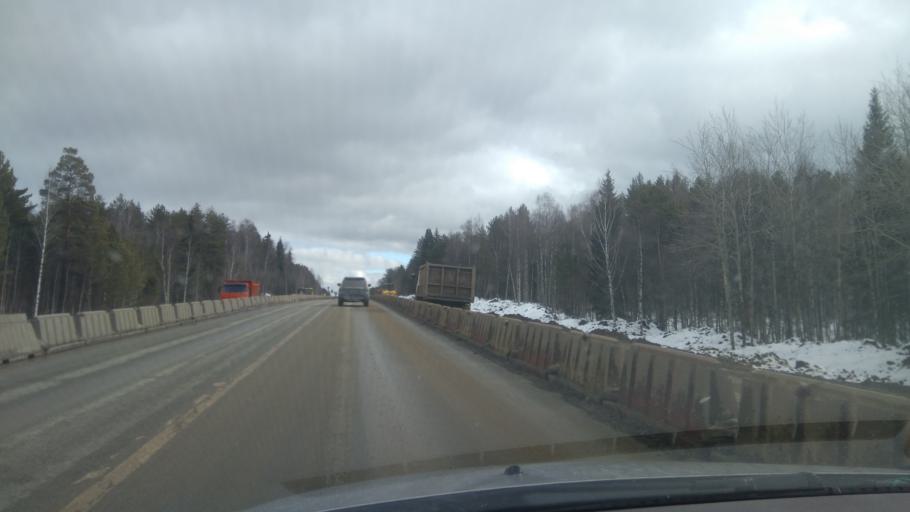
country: RU
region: Sverdlovsk
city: Bisert'
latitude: 56.8338
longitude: 58.9378
